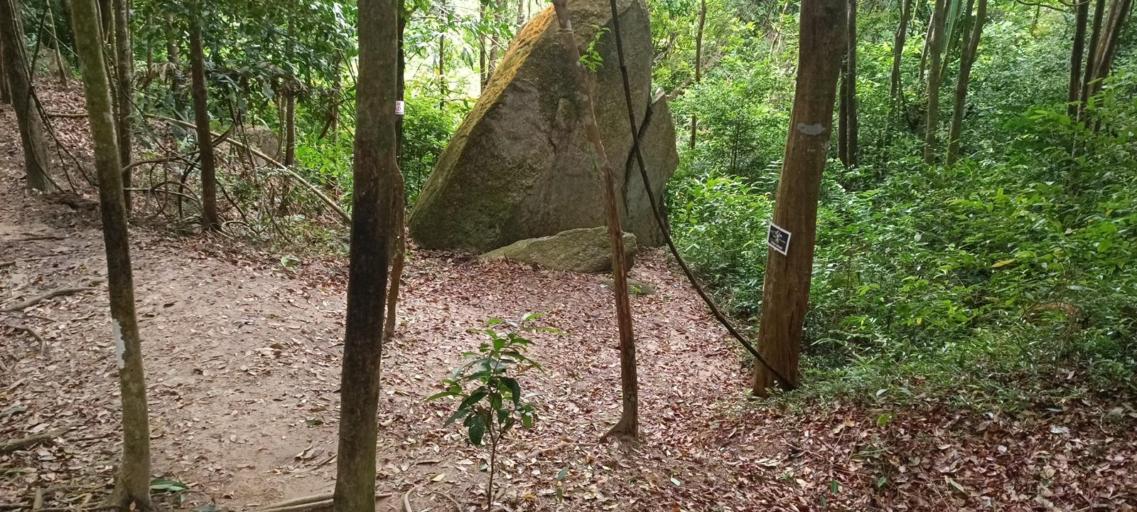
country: MY
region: Penang
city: George Town
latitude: 5.3882
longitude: 100.2902
